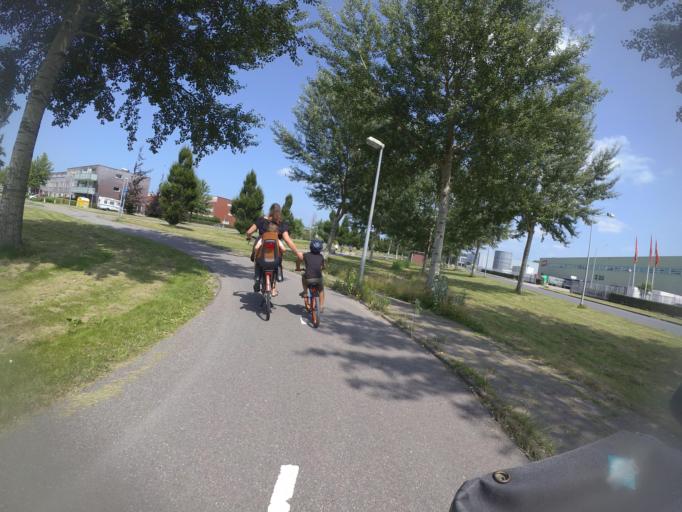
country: NL
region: Flevoland
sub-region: Gemeente Almere
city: Almere Stad
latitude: 52.3676
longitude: 5.2711
